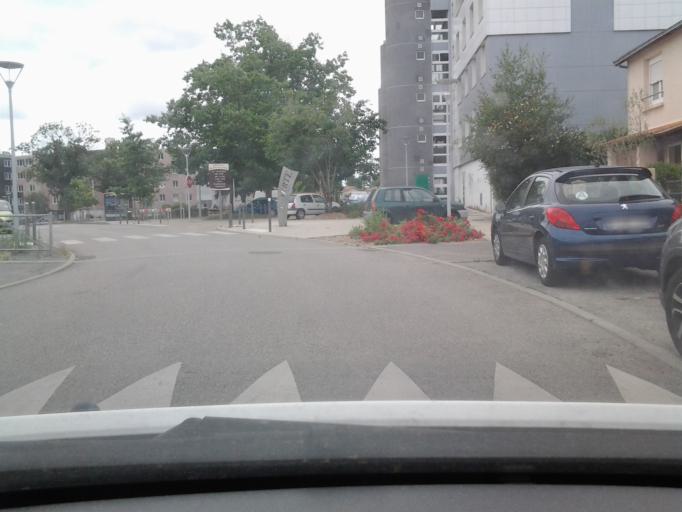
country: FR
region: Pays de la Loire
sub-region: Departement de la Vendee
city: La Roche-sur-Yon
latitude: 46.6630
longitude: -1.4345
